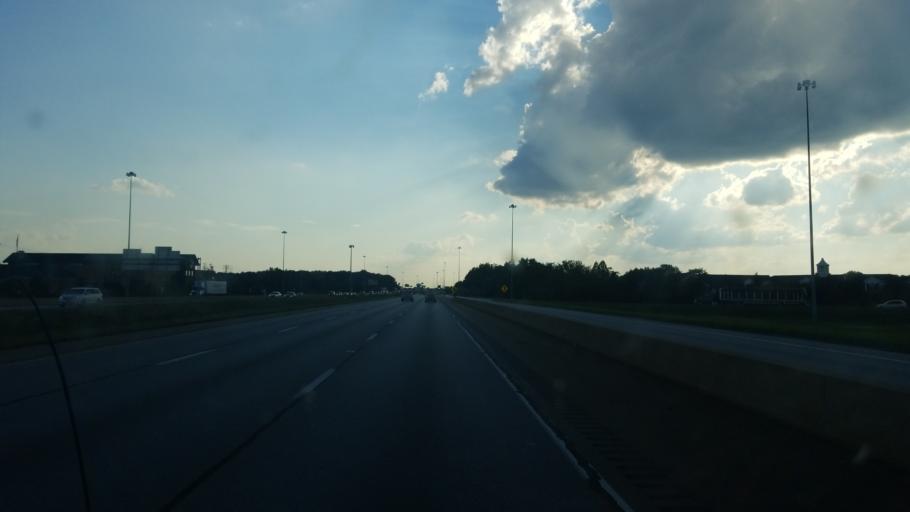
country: US
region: Ohio
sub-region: Wood County
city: Perrysburg
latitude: 41.5637
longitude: -83.5874
